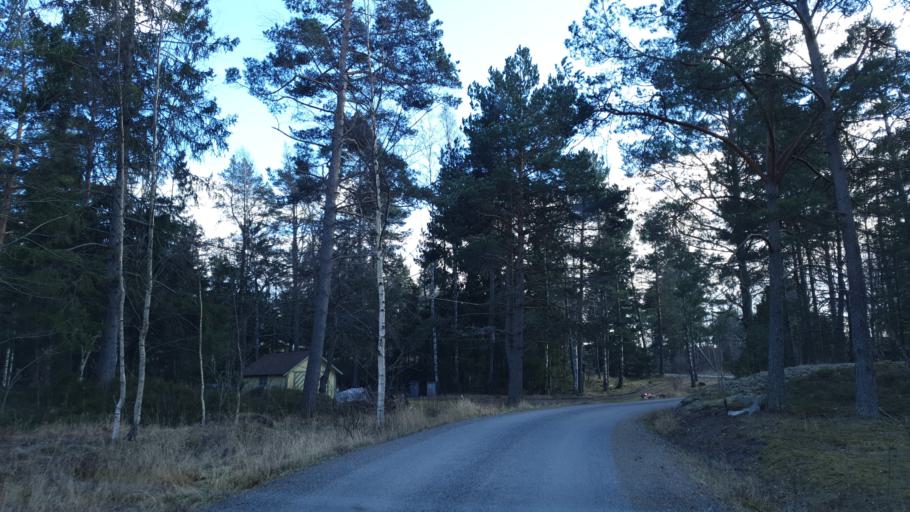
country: SE
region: Stockholm
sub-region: Varmdo Kommun
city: Holo
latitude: 59.2758
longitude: 18.6362
